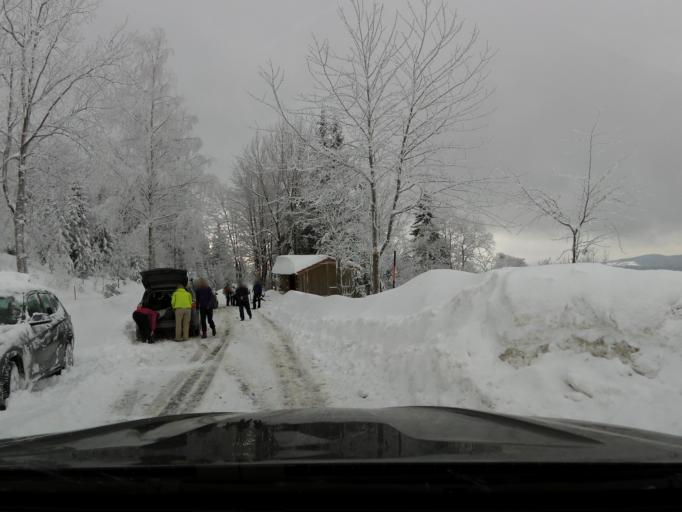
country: DE
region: Bavaria
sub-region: Lower Bavaria
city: Neuschonau
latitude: 48.9276
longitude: 13.4707
